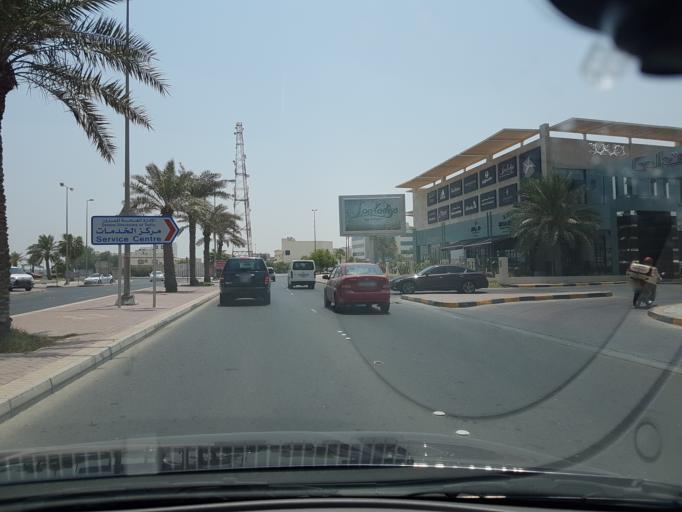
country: BH
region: Manama
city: Manama
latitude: 26.2053
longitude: 50.5756
